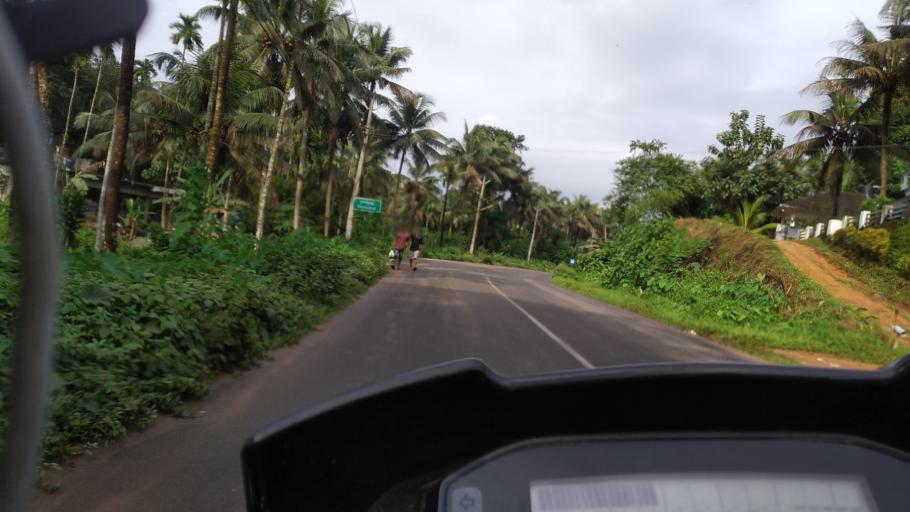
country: IN
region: Kerala
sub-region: Ernakulam
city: Kotamangalam
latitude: 10.0514
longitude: 76.7124
